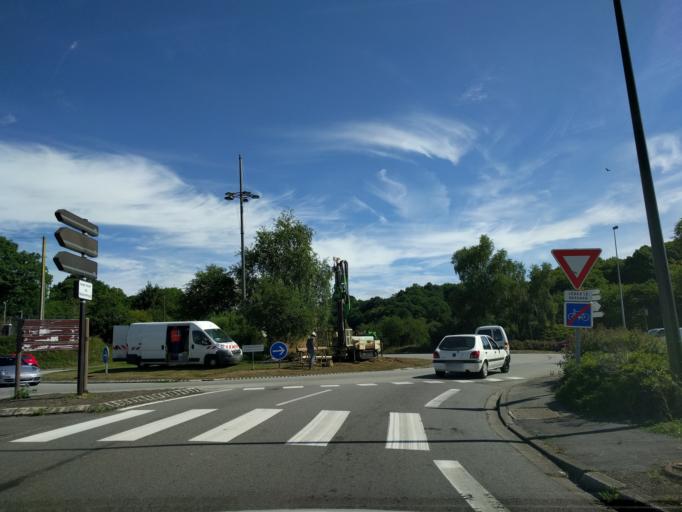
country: FR
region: Brittany
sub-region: Departement du Finistere
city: Quimper
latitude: 48.0032
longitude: -4.0842
